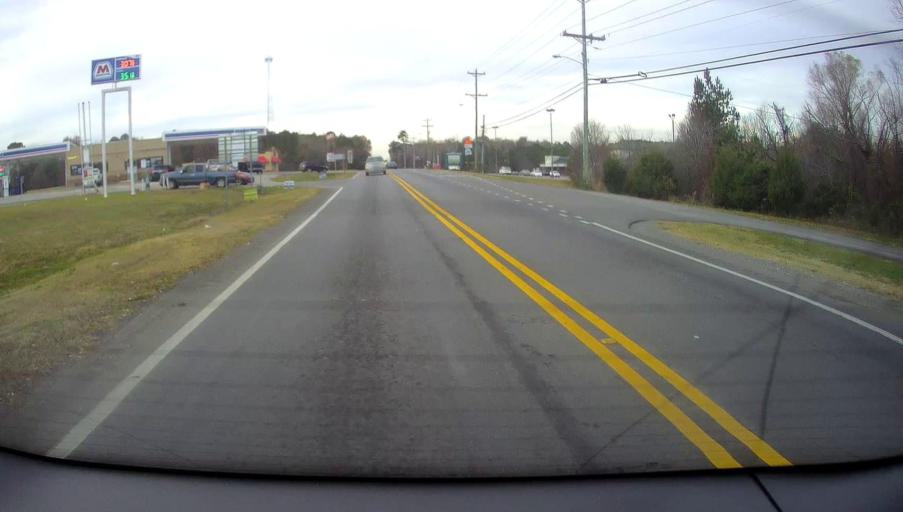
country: US
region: Alabama
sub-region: Morgan County
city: Priceville
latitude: 34.4463
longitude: -86.7565
